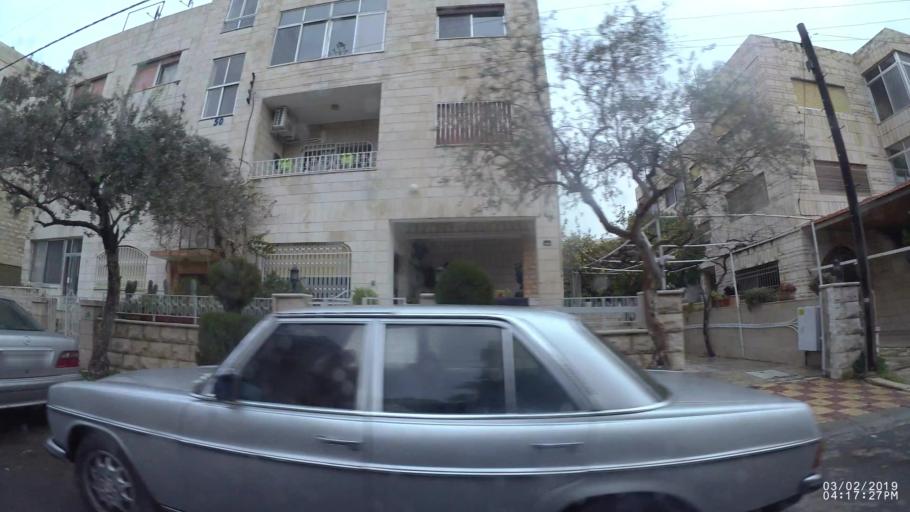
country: JO
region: Amman
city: Amman
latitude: 31.9678
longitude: 35.9136
